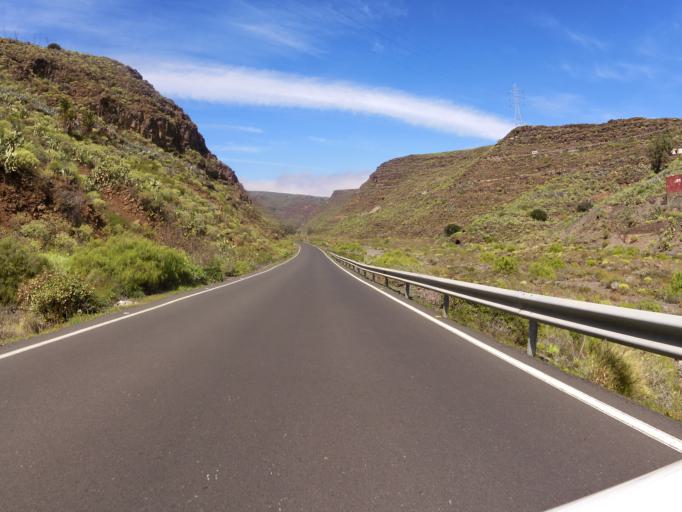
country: ES
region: Canary Islands
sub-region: Provincia de Las Palmas
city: Aguimes
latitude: 27.9160
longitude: -15.4547
